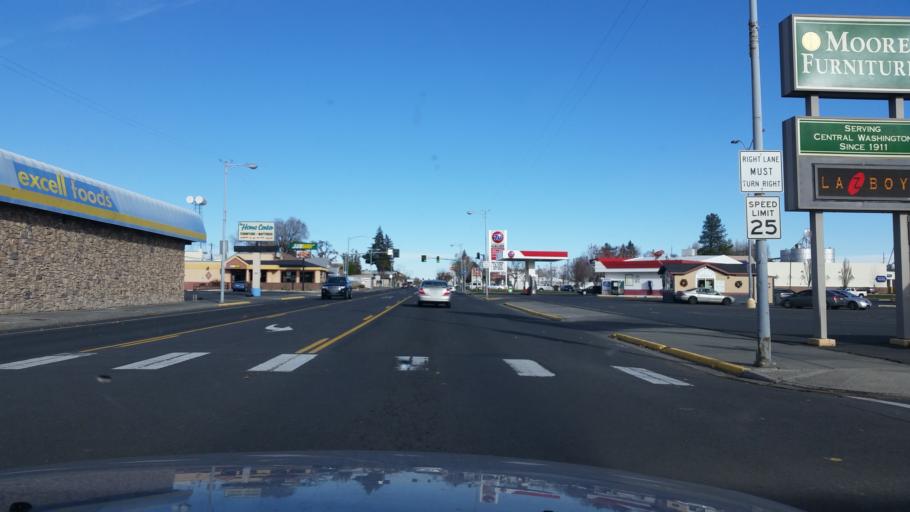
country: US
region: Washington
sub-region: Grant County
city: Ephrata
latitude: 47.3166
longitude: -119.5546
